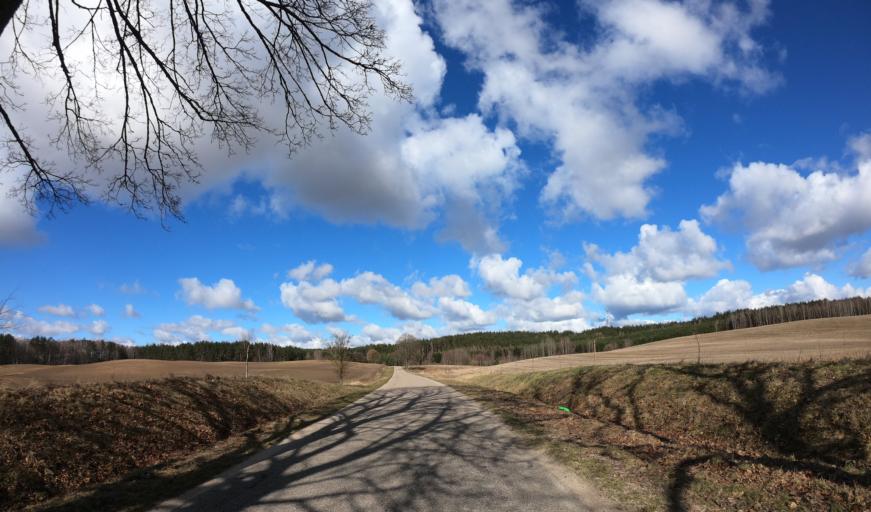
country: PL
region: West Pomeranian Voivodeship
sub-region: Powiat drawski
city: Zlocieniec
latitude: 53.4700
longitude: 15.9293
